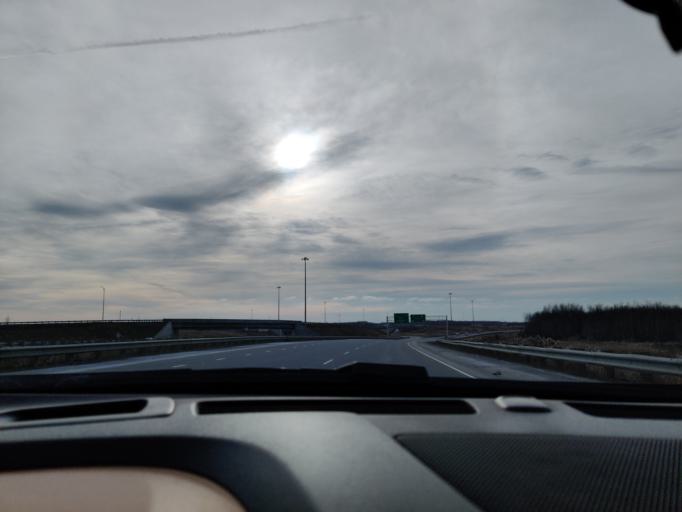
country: CA
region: Quebec
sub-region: Monteregie
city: Vaudreuil-Dorion
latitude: 45.3642
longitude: -74.0497
